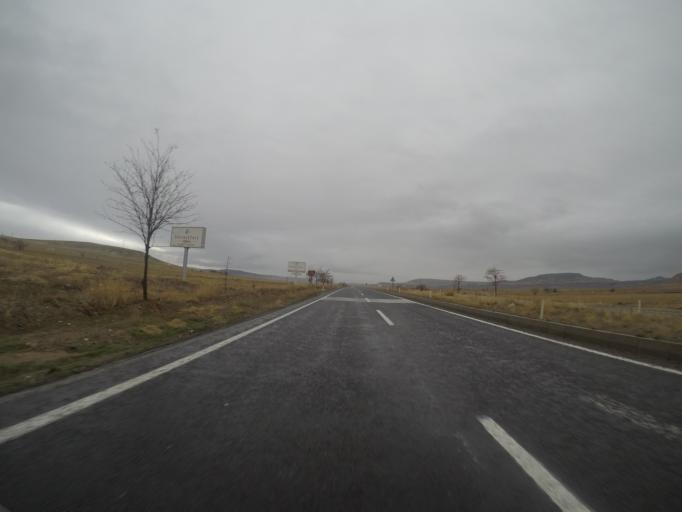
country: TR
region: Nevsehir
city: Avanos
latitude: 38.7152
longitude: 34.9345
